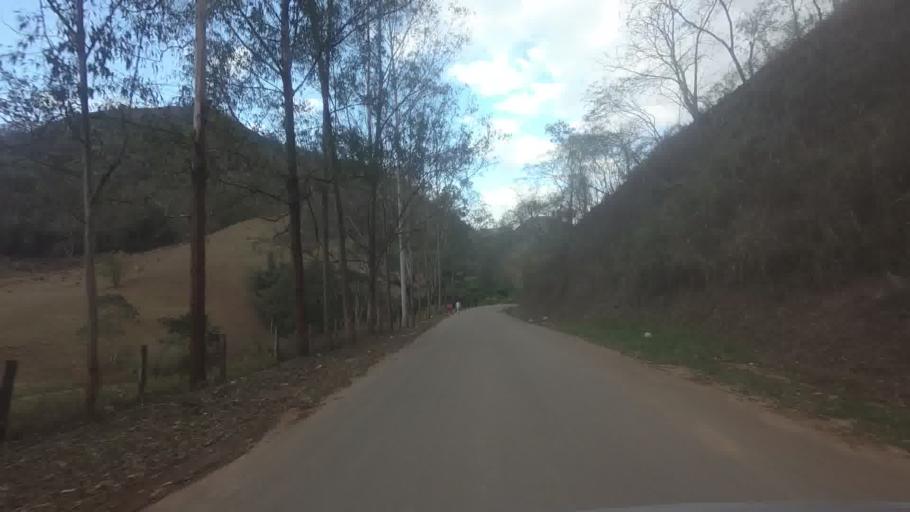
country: BR
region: Espirito Santo
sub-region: Mimoso Do Sul
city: Mimoso do Sul
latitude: -20.9503
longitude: -41.3592
